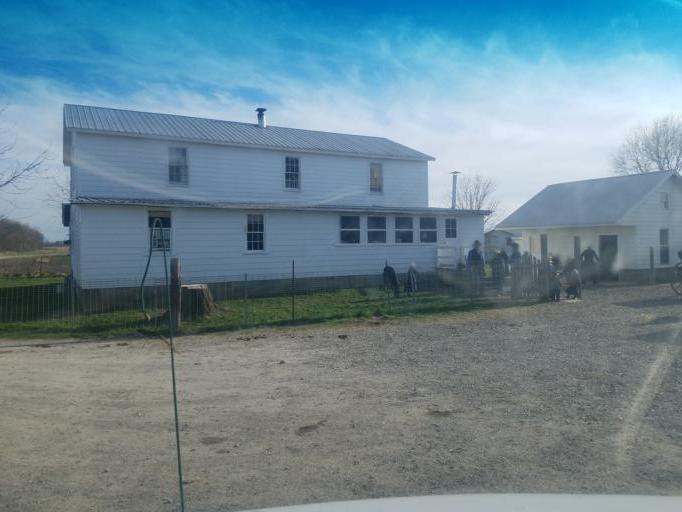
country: US
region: Ohio
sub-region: Logan County
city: De Graff
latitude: 40.3560
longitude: -83.9567
